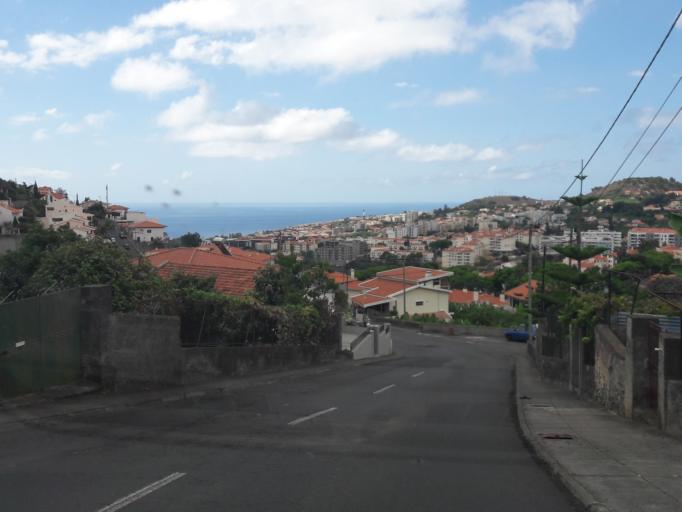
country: PT
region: Madeira
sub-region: Funchal
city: Nossa Senhora do Monte
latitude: 32.6673
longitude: -16.9272
